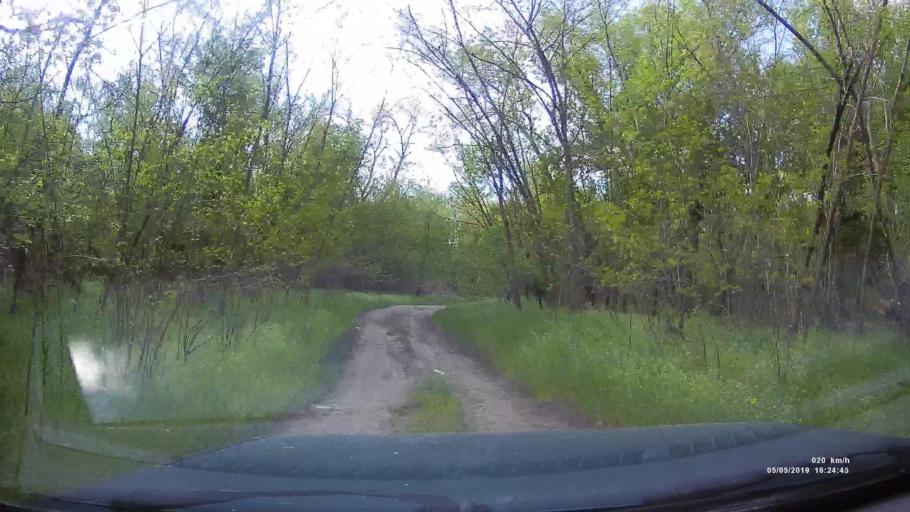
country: RU
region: Rostov
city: Konstantinovsk
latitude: 47.7604
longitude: 41.0249
